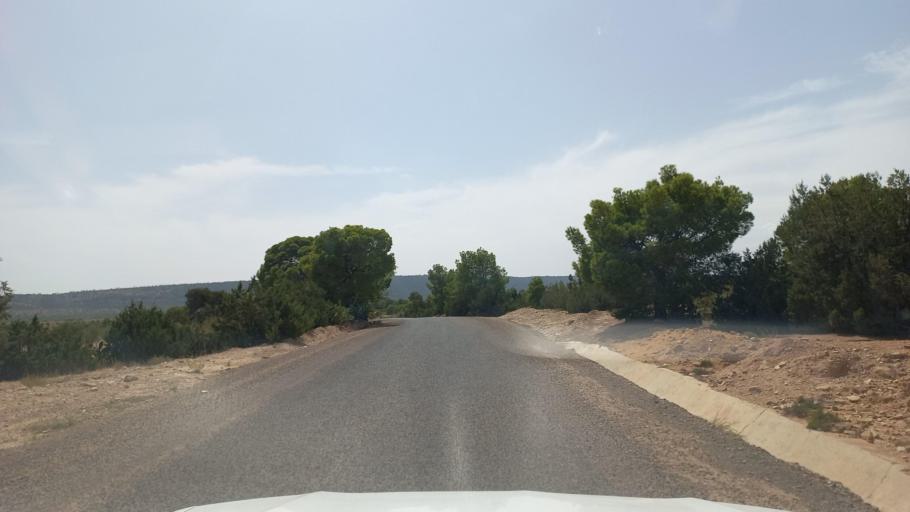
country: TN
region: Al Qasrayn
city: Sbiba
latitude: 35.3964
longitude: 8.9486
